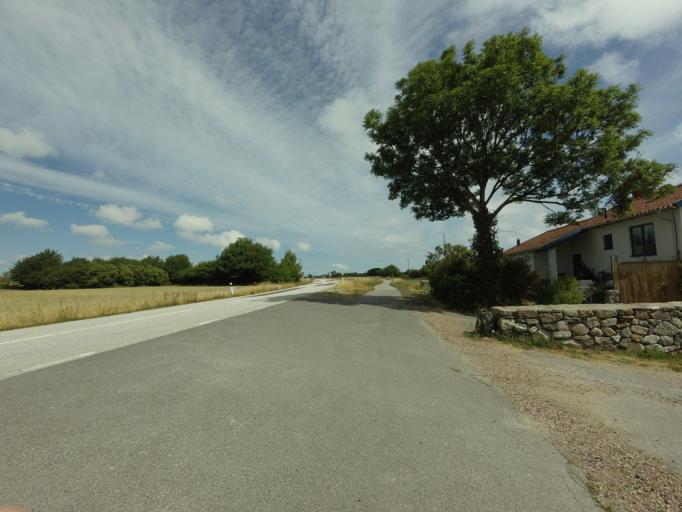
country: SE
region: Skane
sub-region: Simrishamns Kommun
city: Simrishamn
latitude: 55.5092
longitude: 14.3354
